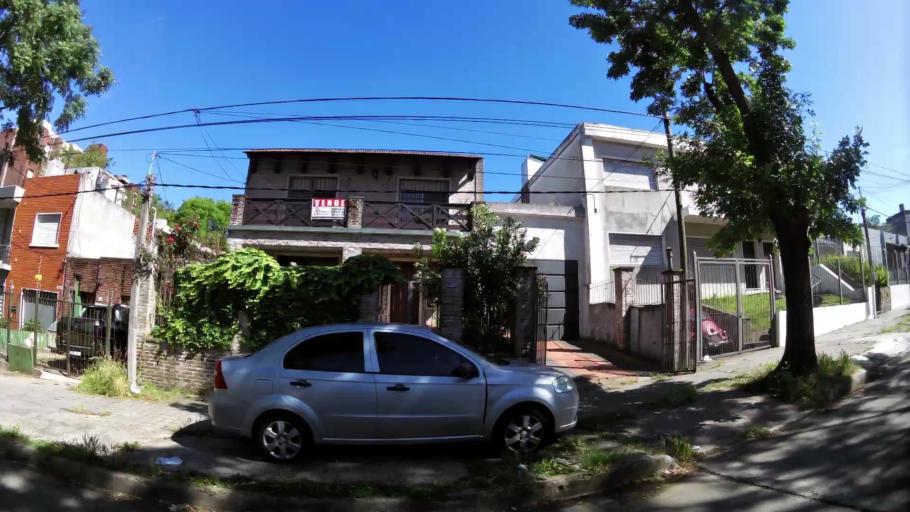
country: UY
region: Montevideo
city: Montevideo
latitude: -34.8899
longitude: -56.1265
